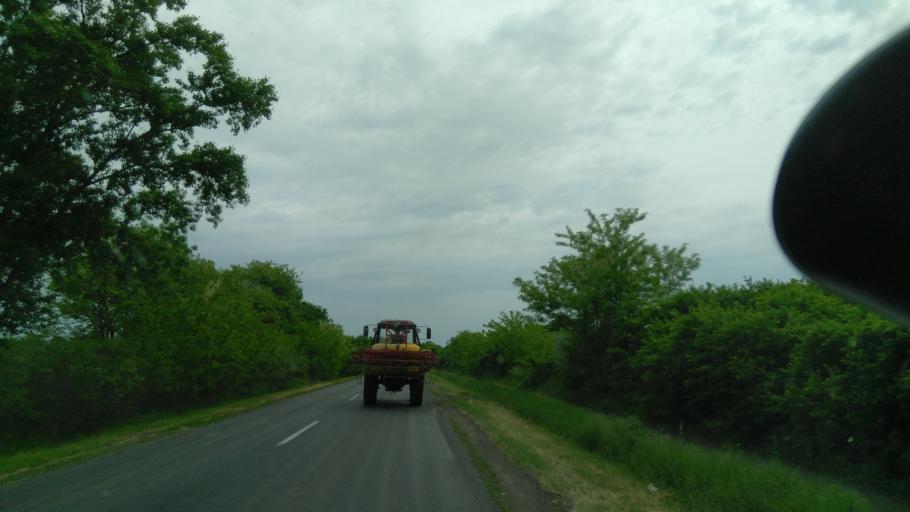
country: HU
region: Bekes
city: Sarkad
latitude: 46.7694
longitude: 21.3820
